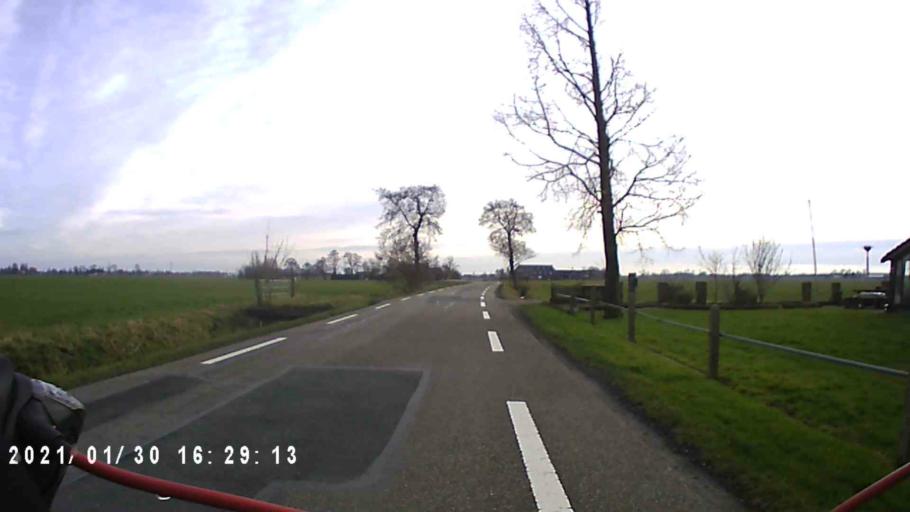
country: NL
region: Groningen
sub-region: Gemeente Zuidhorn
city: Zuidhorn
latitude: 53.2233
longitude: 6.3849
